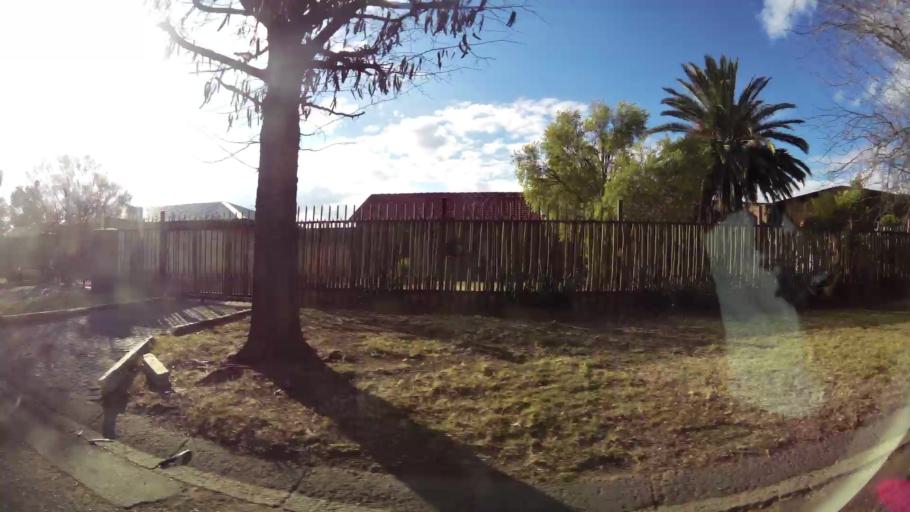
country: ZA
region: Orange Free State
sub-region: Lejweleputswa District Municipality
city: Welkom
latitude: -27.9800
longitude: 26.7000
